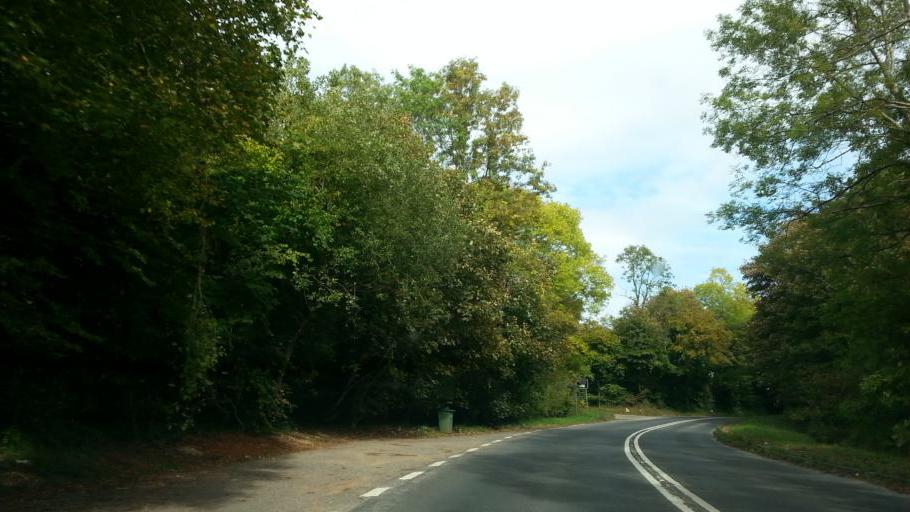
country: GB
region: England
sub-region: Gloucestershire
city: Painswick
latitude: 51.8039
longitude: -2.1905
